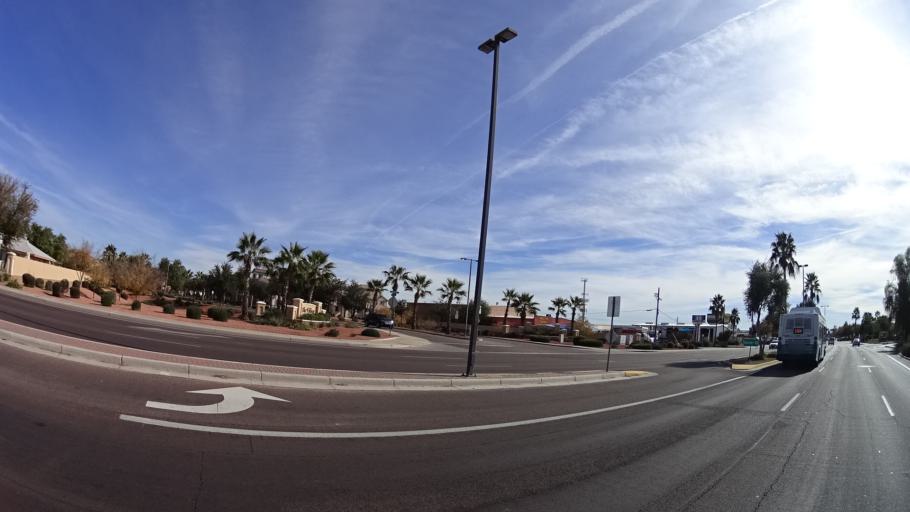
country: US
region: Arizona
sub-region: Maricopa County
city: Gilbert
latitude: 33.3383
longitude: -111.7899
